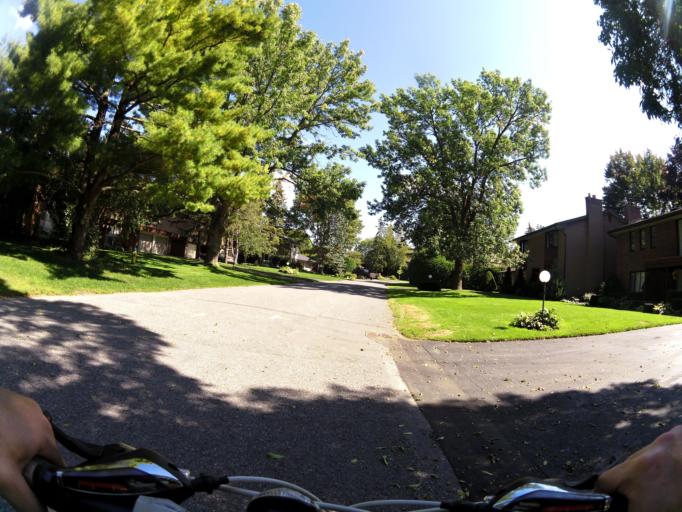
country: CA
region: Ontario
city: Bells Corners
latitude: 45.3258
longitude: -75.9065
